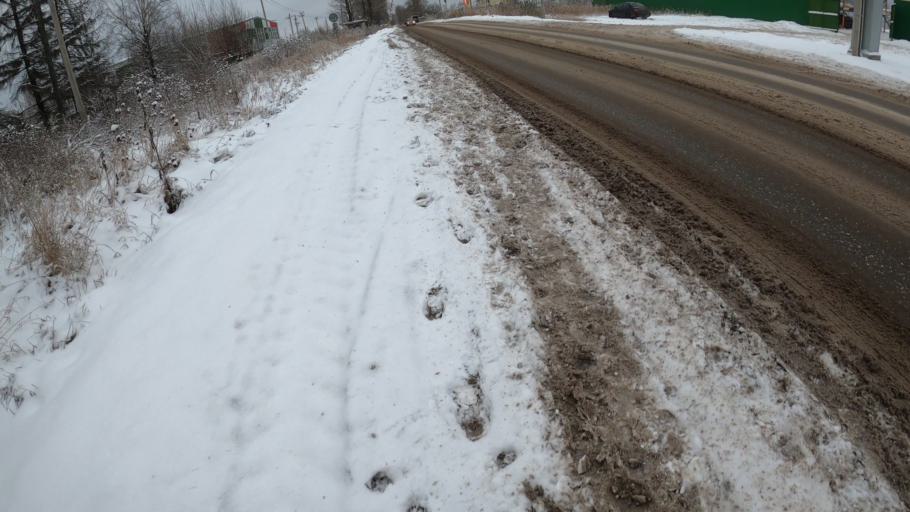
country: RU
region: Jaroslavl
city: Pereslavl'-Zalesskiy
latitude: 56.7382
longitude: 38.8997
